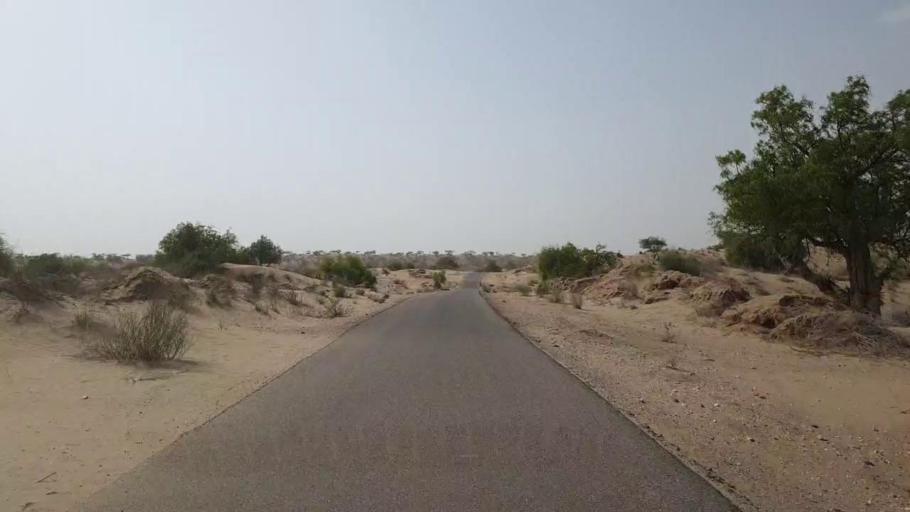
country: PK
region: Sindh
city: Mithi
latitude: 24.5795
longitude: 69.9242
